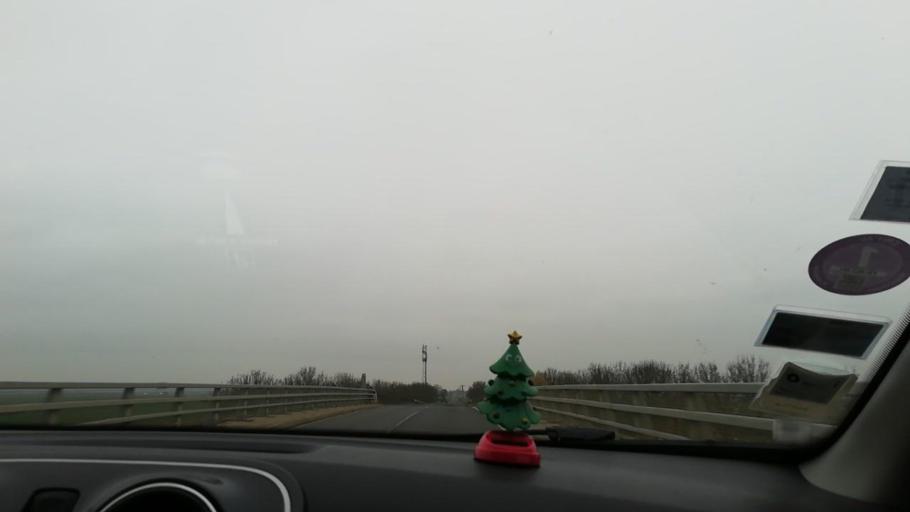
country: FR
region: Ile-de-France
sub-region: Departement de Seine-et-Marne
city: Charny
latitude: 48.9685
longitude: 2.7320
